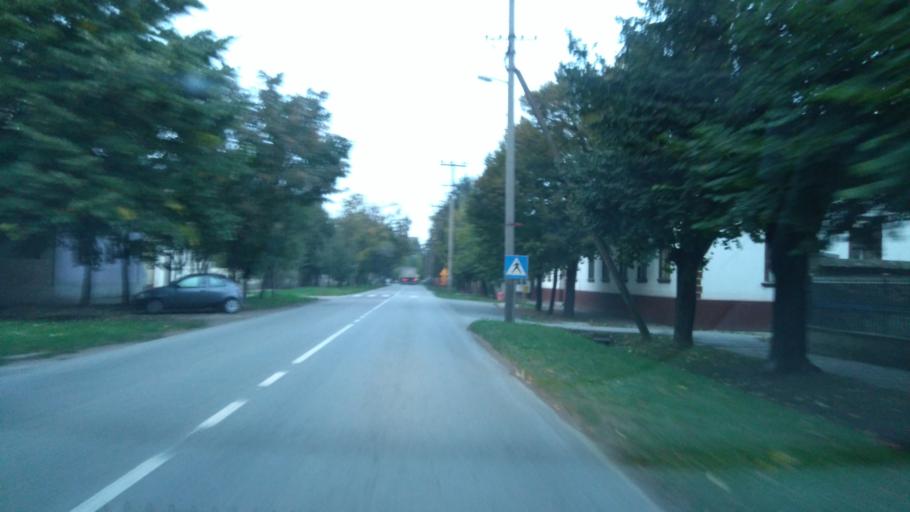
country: RS
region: Autonomna Pokrajina Vojvodina
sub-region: Severnobanatski Okrug
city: Ada
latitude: 45.7935
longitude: 20.1376
